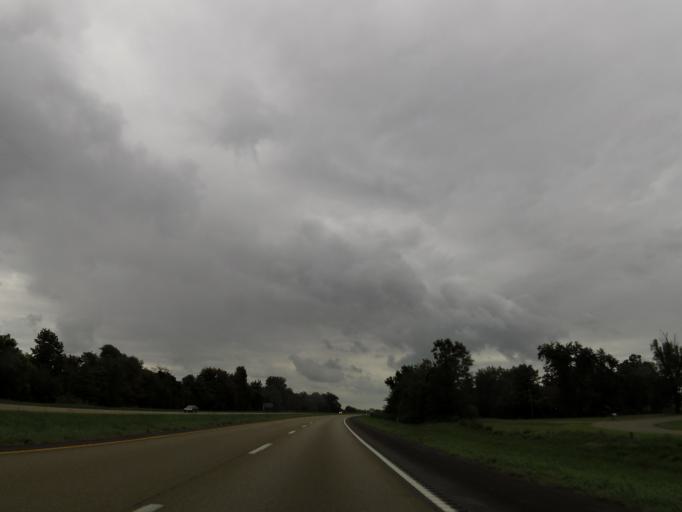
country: US
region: Missouri
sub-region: Mississippi County
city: Charleston
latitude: 36.9062
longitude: -89.4392
